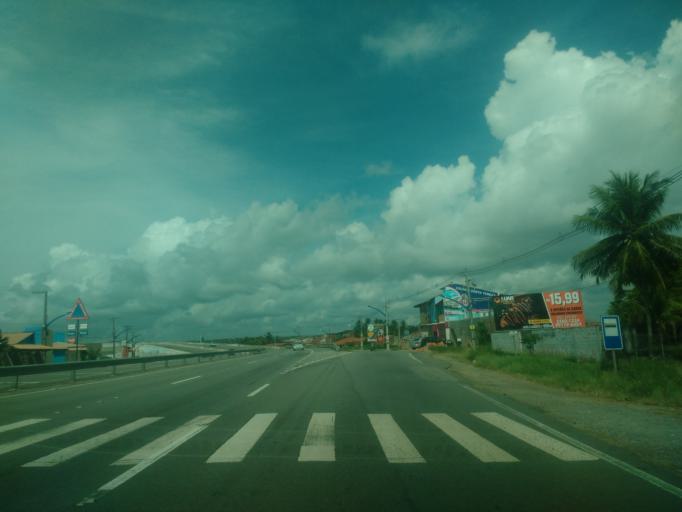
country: BR
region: Alagoas
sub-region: Marechal Deodoro
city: Marechal Deodoro
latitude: -9.7648
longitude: -35.8481
